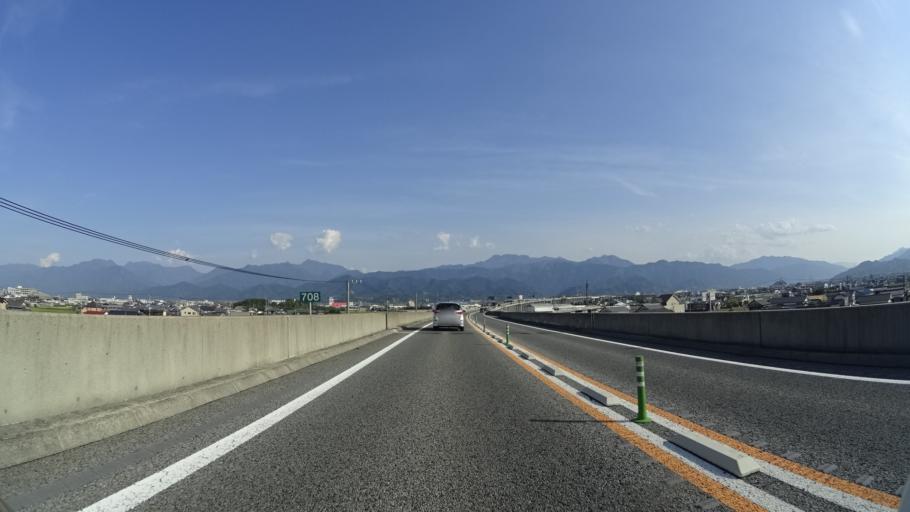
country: JP
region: Ehime
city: Saijo
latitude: 33.9275
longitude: 133.0739
